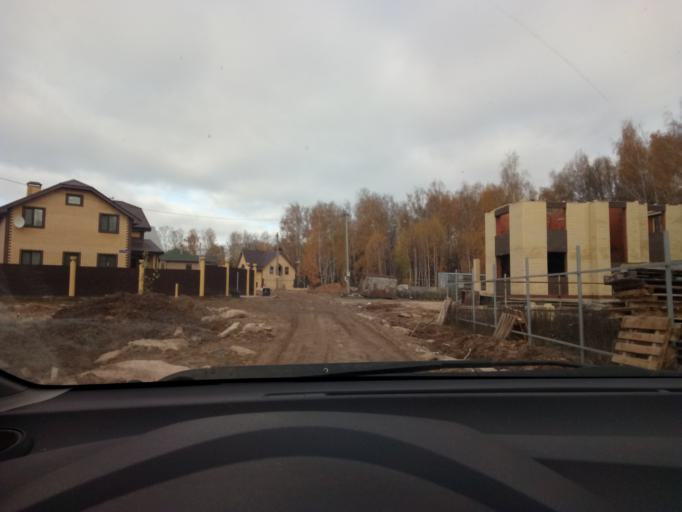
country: RU
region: Tatarstan
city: Staroye Arakchino
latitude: 55.9697
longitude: 49.0450
